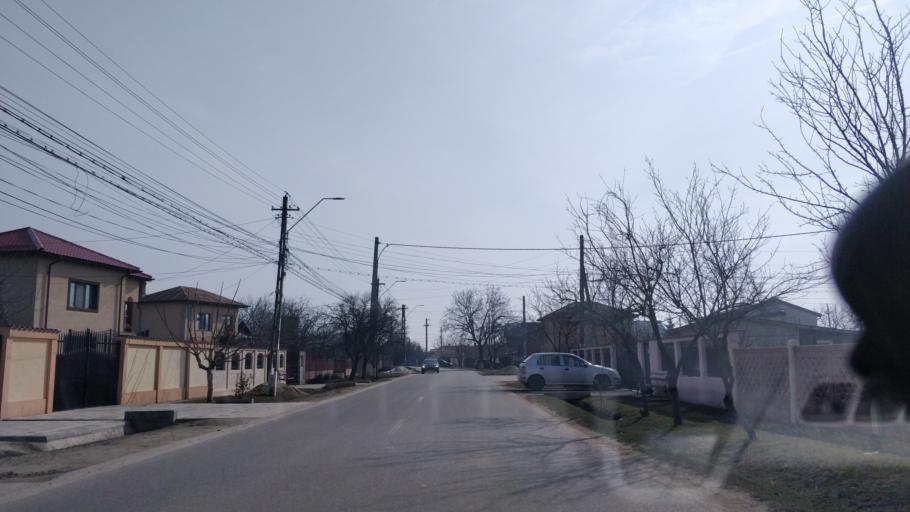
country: RO
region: Giurgiu
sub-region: Comuna Ulmi
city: Ulmi
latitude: 44.4854
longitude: 25.7833
